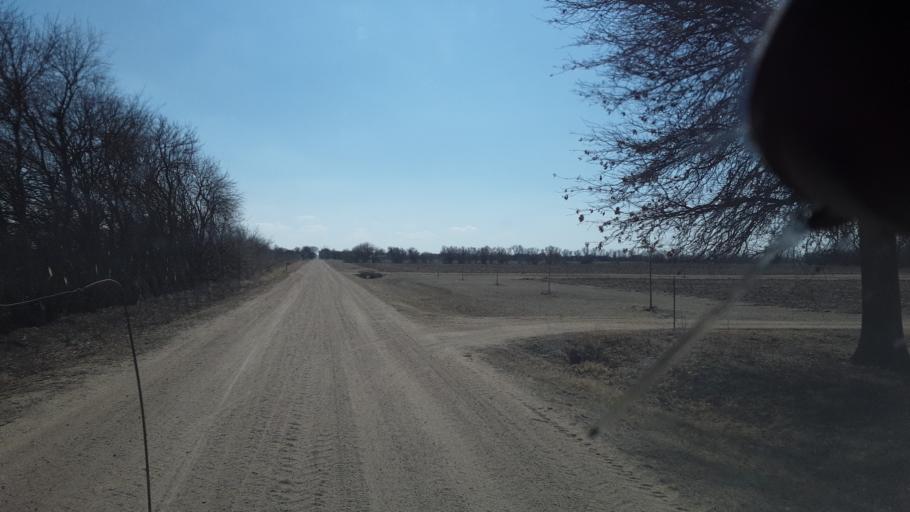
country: US
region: Kansas
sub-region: Reno County
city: Haven
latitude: 37.9256
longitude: -97.8485
